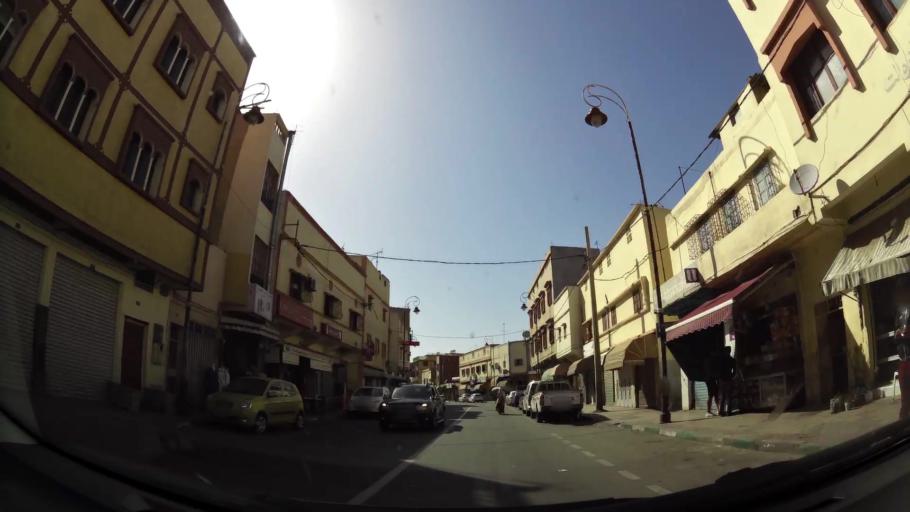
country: MA
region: Souss-Massa-Draa
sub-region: Inezgane-Ait Mellou
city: Inezgane
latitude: 30.3714
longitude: -9.5419
